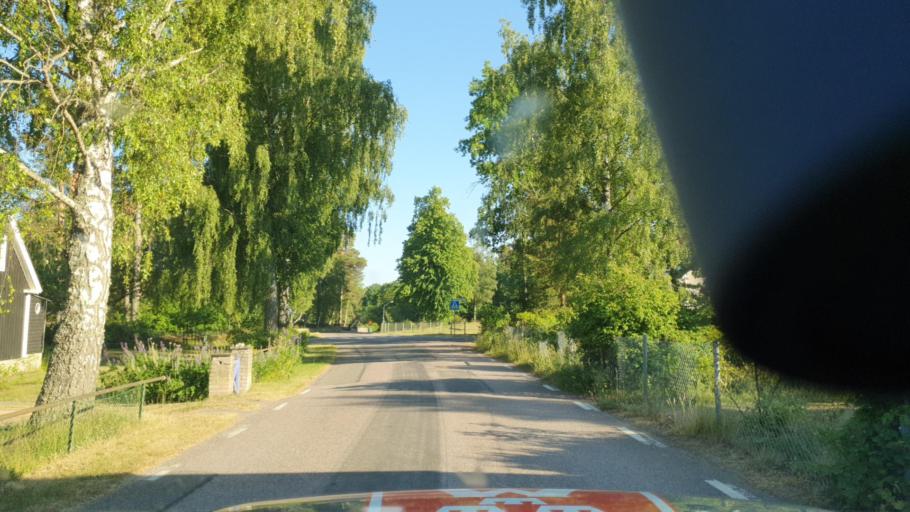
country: SE
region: Kalmar
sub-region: Torsas Kommun
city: Torsas
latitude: 56.4979
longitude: 16.1021
